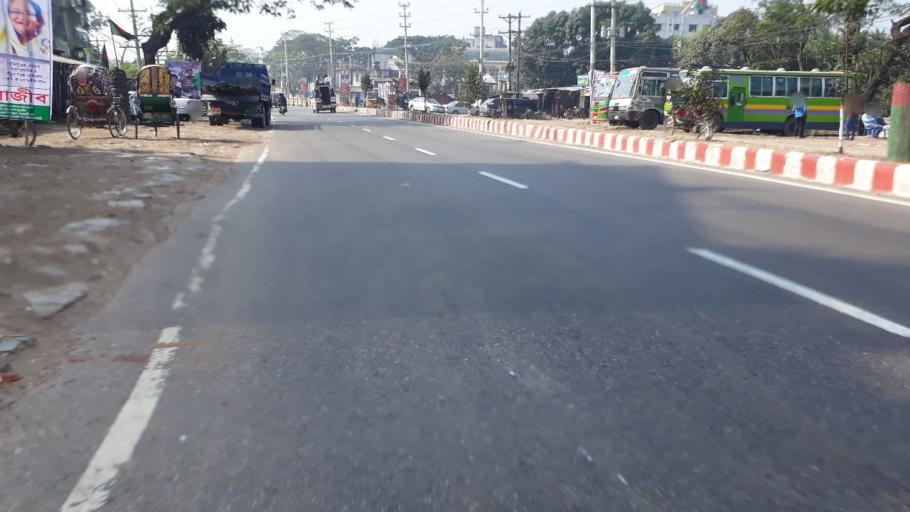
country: BD
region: Dhaka
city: Tungi
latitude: 23.8608
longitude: 90.2645
